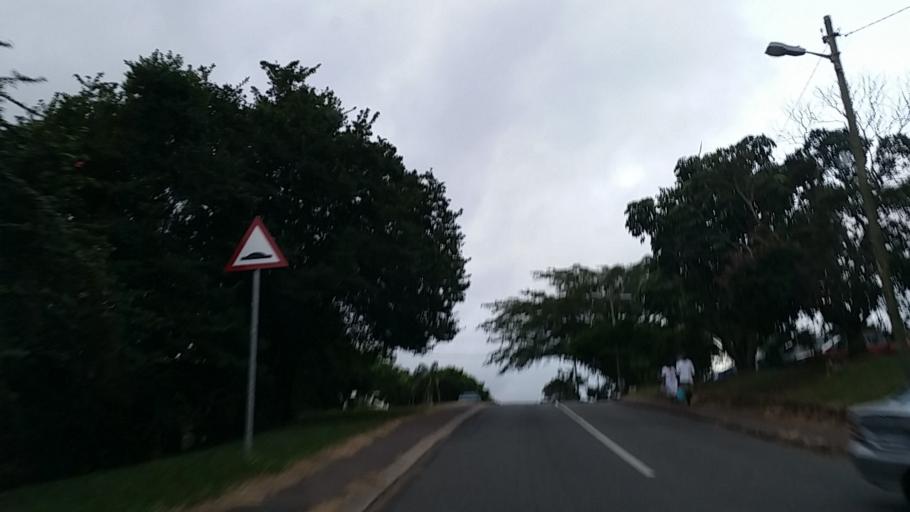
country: ZA
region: KwaZulu-Natal
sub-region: eThekwini Metropolitan Municipality
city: Berea
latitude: -29.8423
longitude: 30.9055
